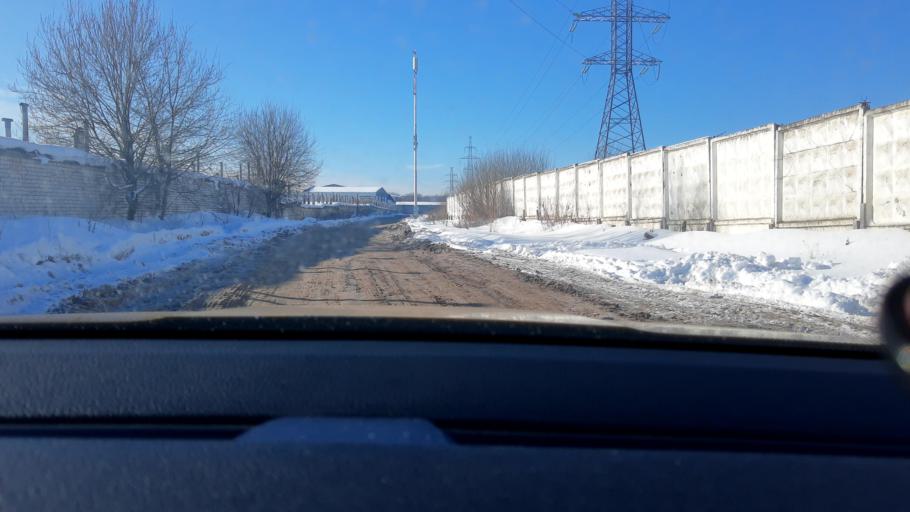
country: RU
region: Moskovskaya
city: Odintsovo
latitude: 55.6751
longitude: 37.2377
